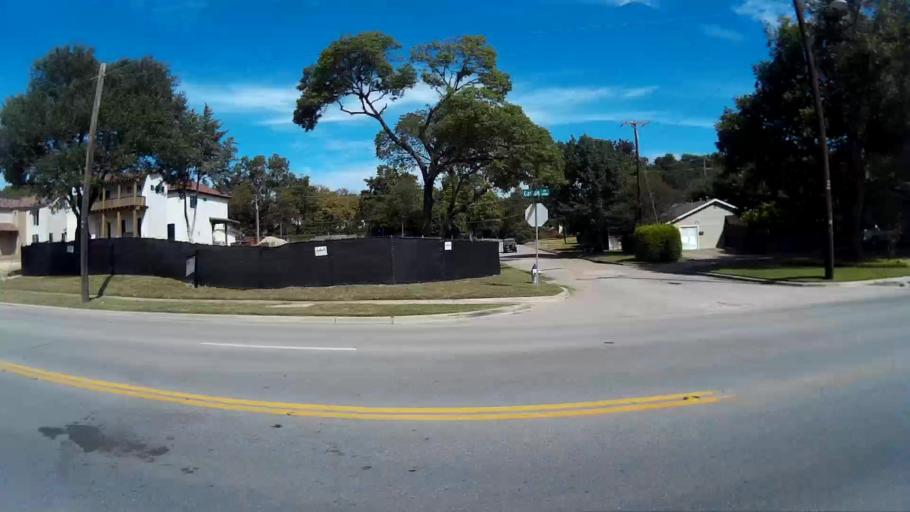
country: US
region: Texas
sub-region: Dallas County
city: Highland Park
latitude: 32.8162
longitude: -96.7440
